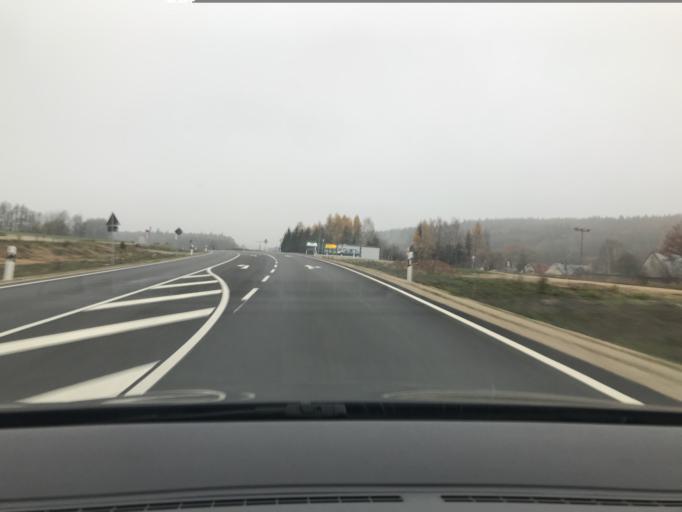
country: DE
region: Bavaria
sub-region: Regierungsbezirk Mittelfranken
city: Wilburgstetten
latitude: 49.0094
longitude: 10.4095
